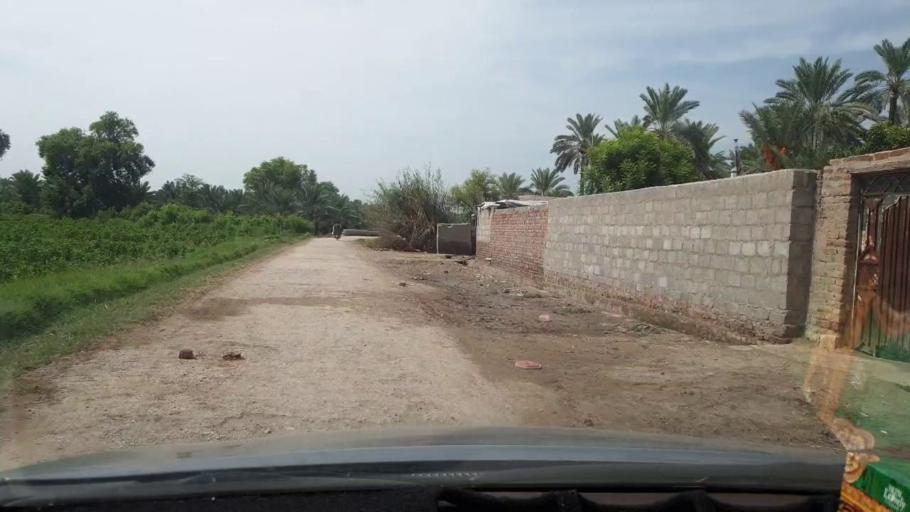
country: PK
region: Sindh
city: Khairpur
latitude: 27.4912
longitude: 68.7544
